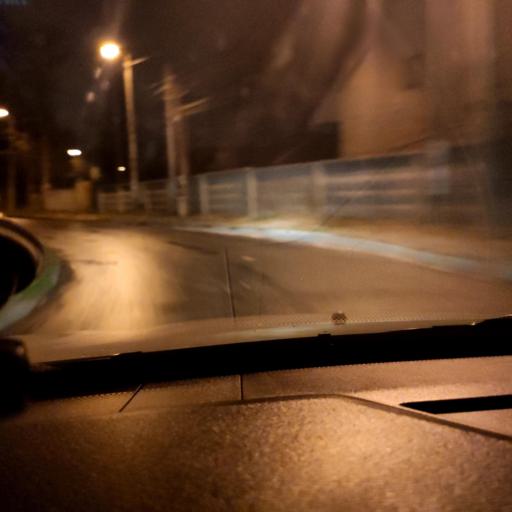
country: RU
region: Samara
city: Samara
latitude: 53.2872
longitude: 50.1986
